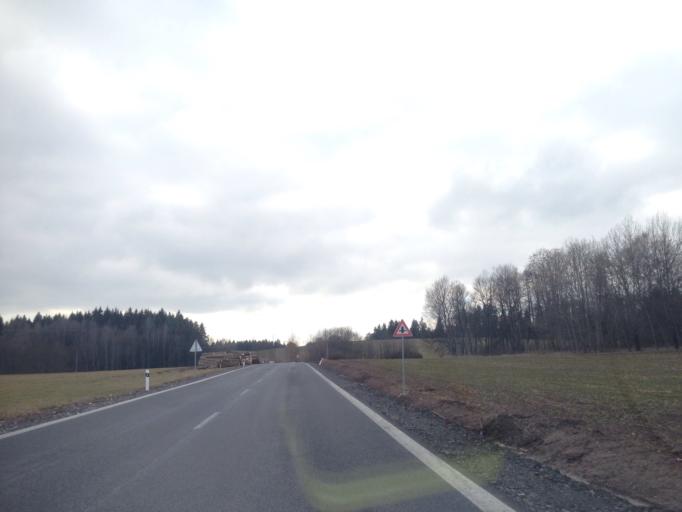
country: CZ
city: Horni Branna
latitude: 50.5840
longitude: 15.5773
